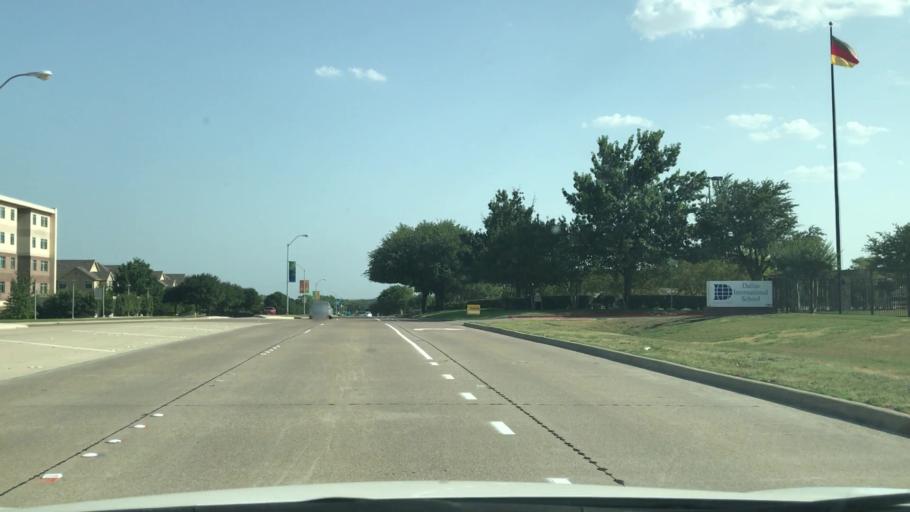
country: US
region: Texas
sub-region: Dallas County
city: Richardson
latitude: 32.9912
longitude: -96.7565
